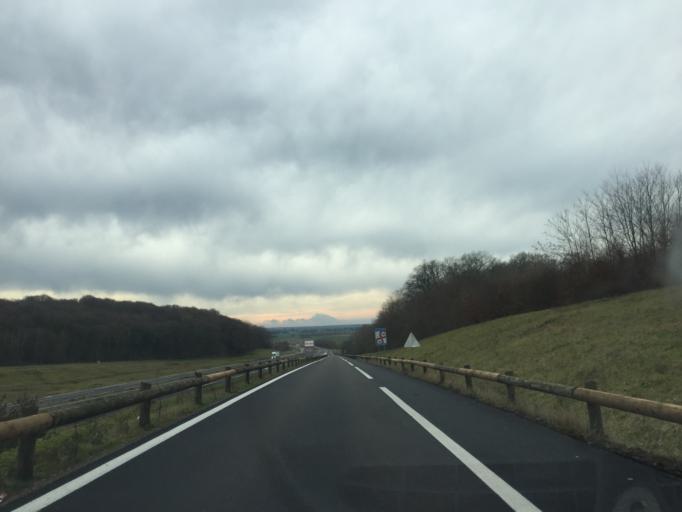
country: FR
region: Franche-Comte
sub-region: Departement du Jura
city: Bletterans
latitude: 46.7766
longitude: 5.5200
